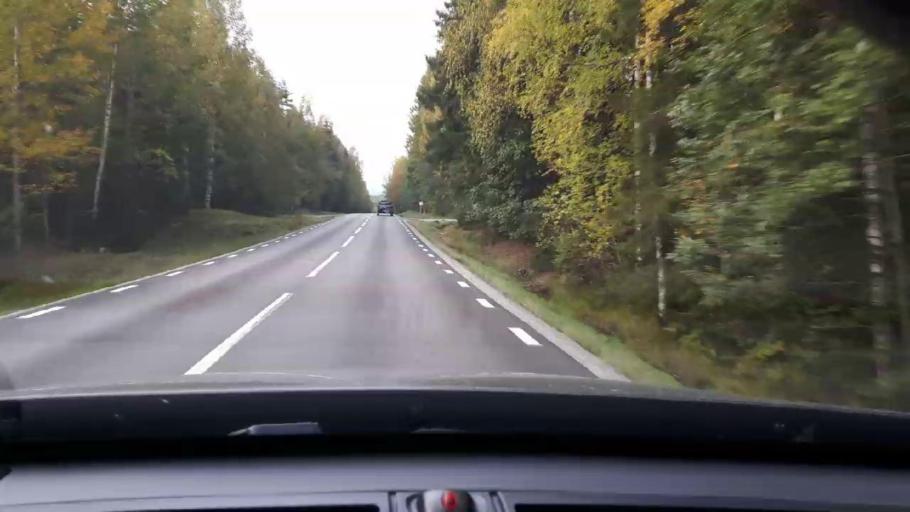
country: SE
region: Dalarna
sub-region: Ludvika Kommun
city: Grangesberg
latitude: 60.2287
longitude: 15.0403
